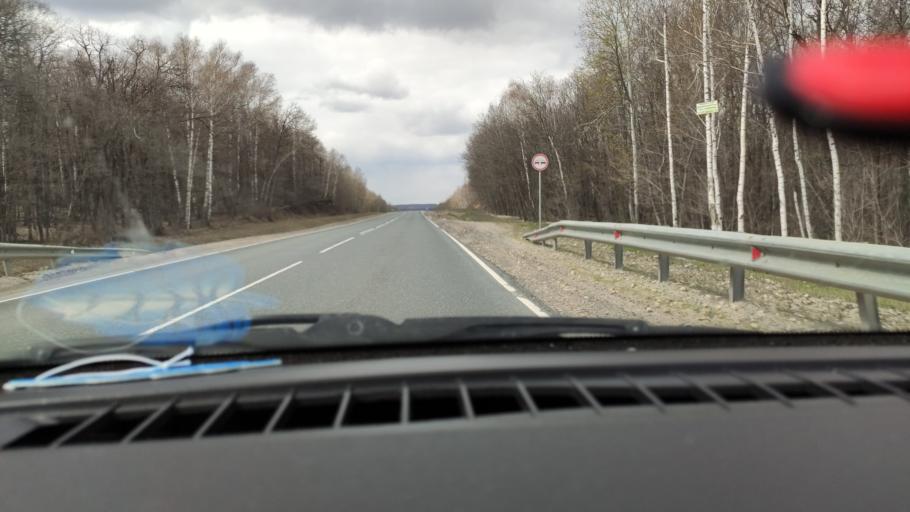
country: RU
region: Saratov
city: Vol'sk
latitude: 52.1124
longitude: 47.3221
